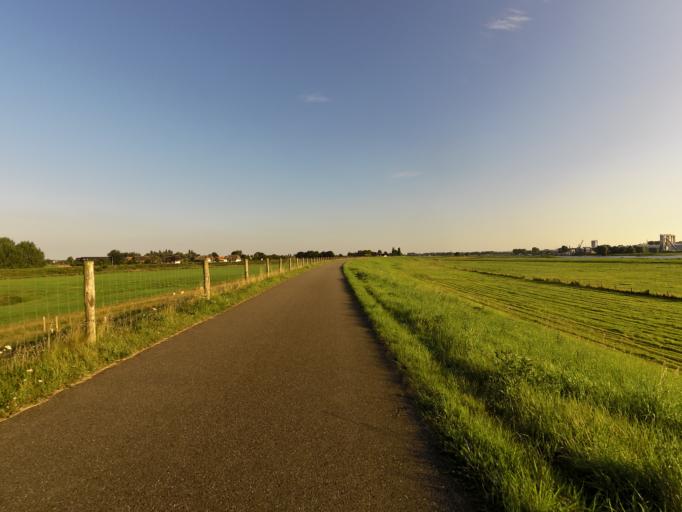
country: NL
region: Gelderland
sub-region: Gemeente Westervoort
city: Westervoort
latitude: 51.9462
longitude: 5.9645
